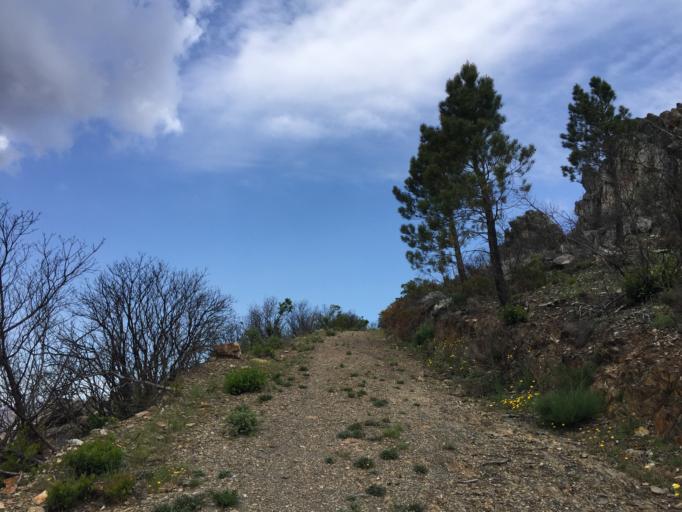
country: PT
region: Coimbra
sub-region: Pampilhosa da Serra
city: Pampilhosa da Serra
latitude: 40.1603
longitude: -7.9291
